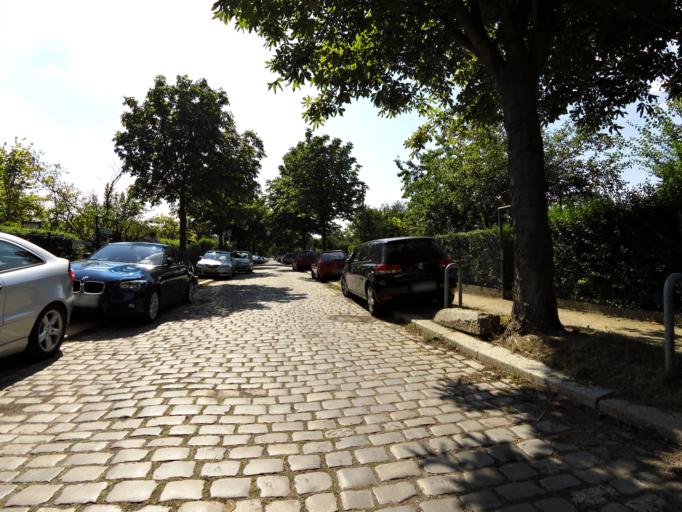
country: DE
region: Berlin
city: Schoneberg Bezirk
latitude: 52.4630
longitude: 13.3557
